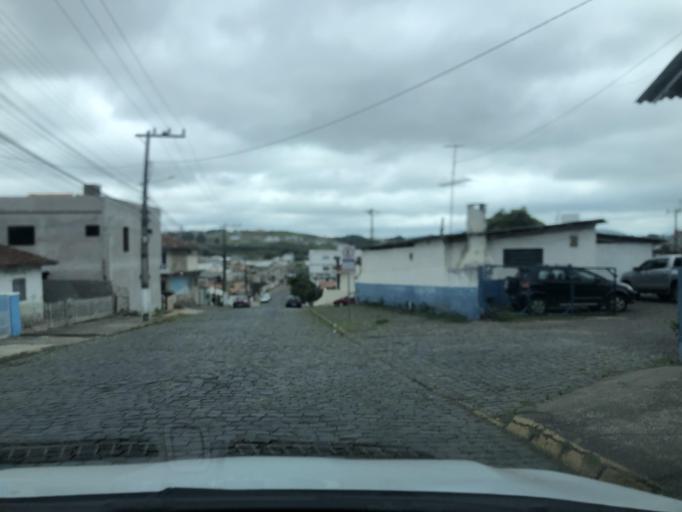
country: BR
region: Santa Catarina
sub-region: Lages
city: Lages
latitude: -27.8075
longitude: -50.3038
